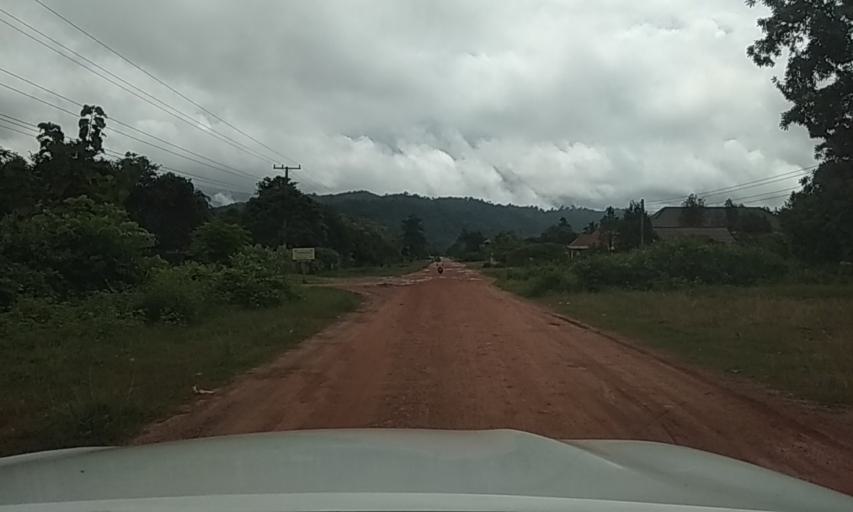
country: LA
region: Bolikhamxai
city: Bolikhan
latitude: 18.5571
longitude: 103.7323
